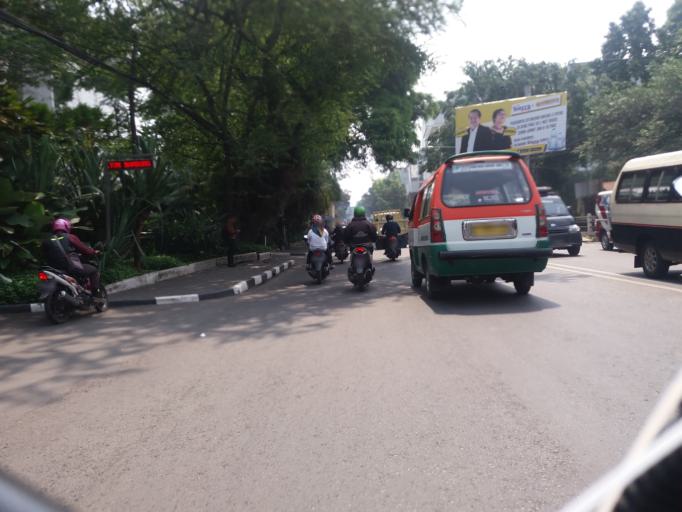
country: ID
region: West Java
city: Bandung
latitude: -6.9131
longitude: 107.5980
